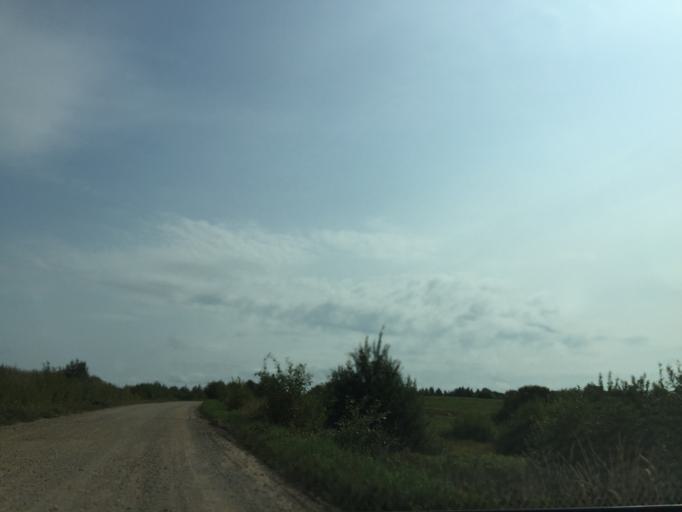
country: LV
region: Ludzas Rajons
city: Ludza
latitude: 56.2772
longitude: 27.7849
